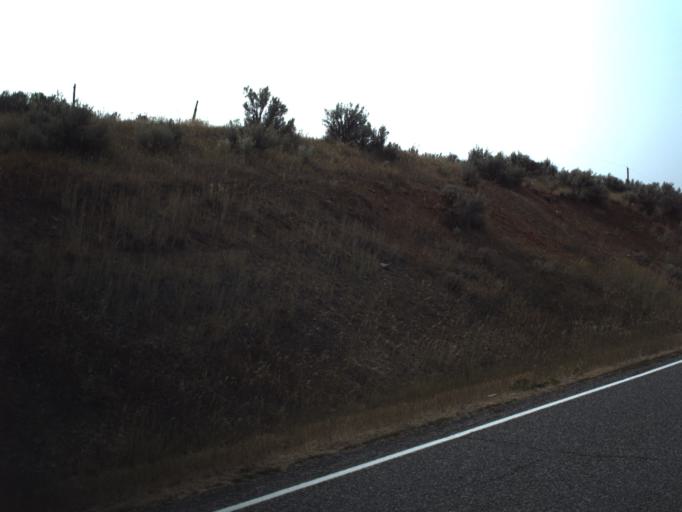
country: US
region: Utah
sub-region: Summit County
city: Coalville
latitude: 40.9954
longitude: -111.5244
